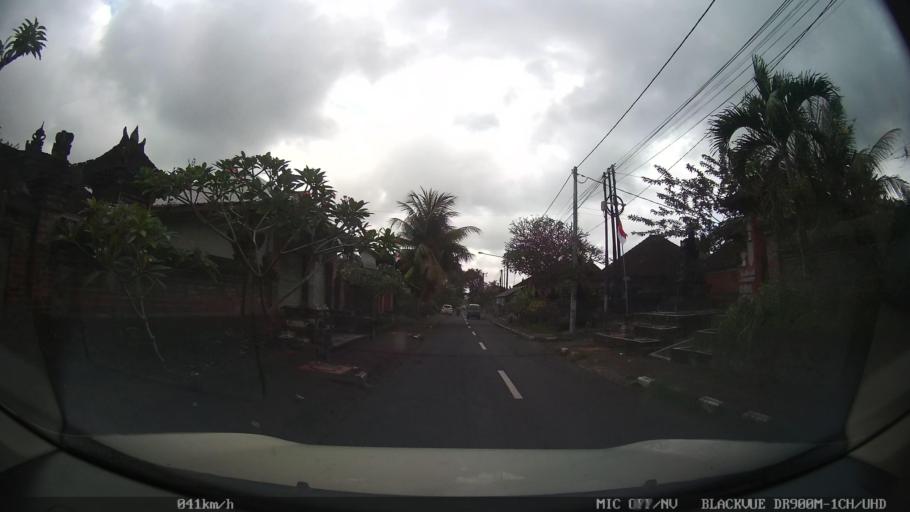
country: ID
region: Bali
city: Banjar Kembangsari
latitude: -8.5149
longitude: 115.2058
